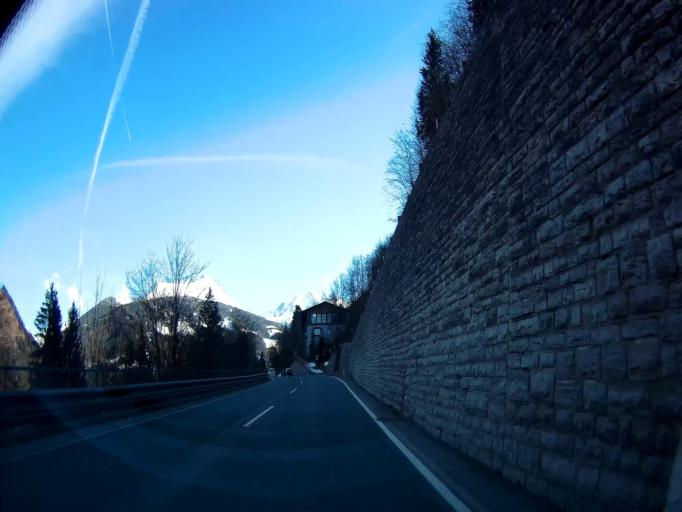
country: AT
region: Salzburg
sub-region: Politischer Bezirk Sankt Johann im Pongau
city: Bad Gastein
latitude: 47.1353
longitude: 13.1268
